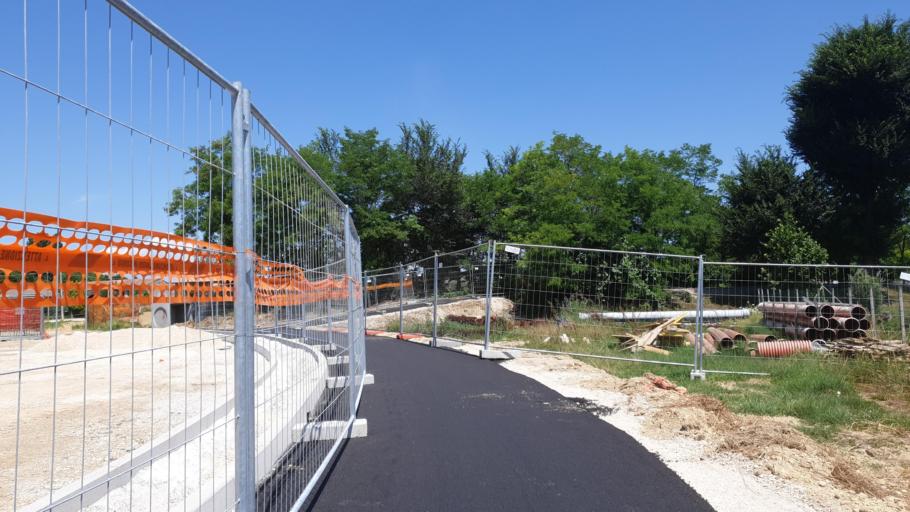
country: IT
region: Veneto
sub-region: Provincia di Padova
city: Pieve
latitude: 45.5457
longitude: 11.8491
